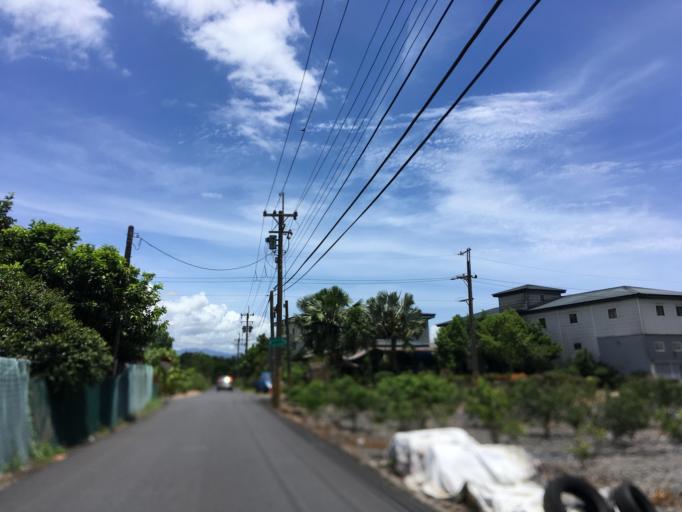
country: TW
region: Taiwan
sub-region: Yilan
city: Yilan
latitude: 24.6400
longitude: 121.7198
